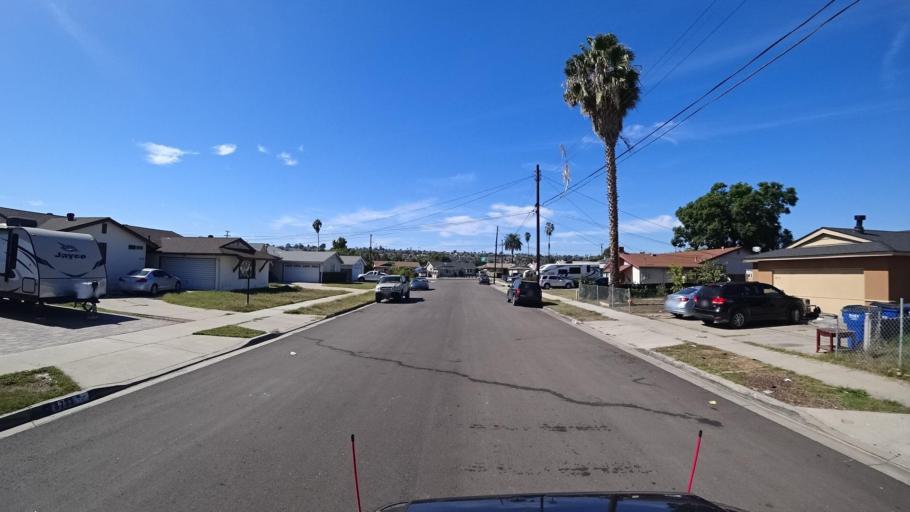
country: US
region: California
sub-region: San Diego County
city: La Presa
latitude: 32.7107
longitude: -117.0104
